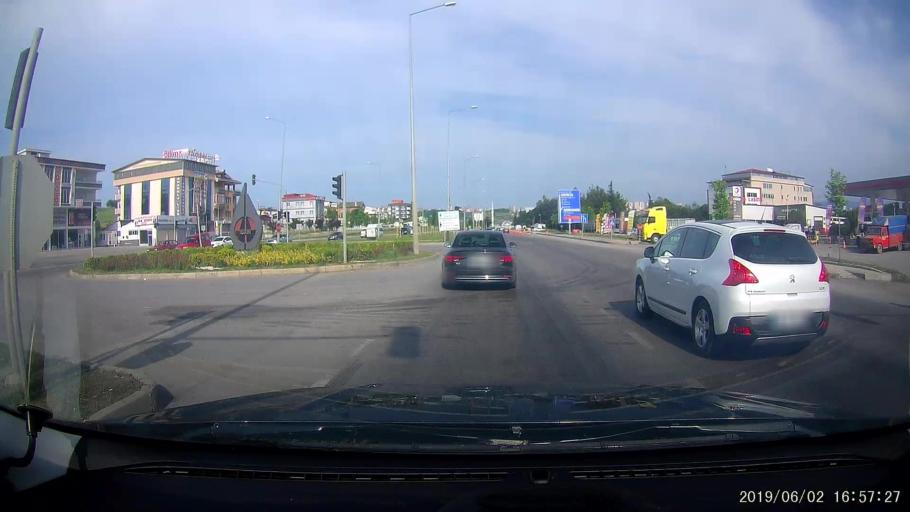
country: TR
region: Samsun
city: Samsun
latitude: 41.2909
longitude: 36.2740
